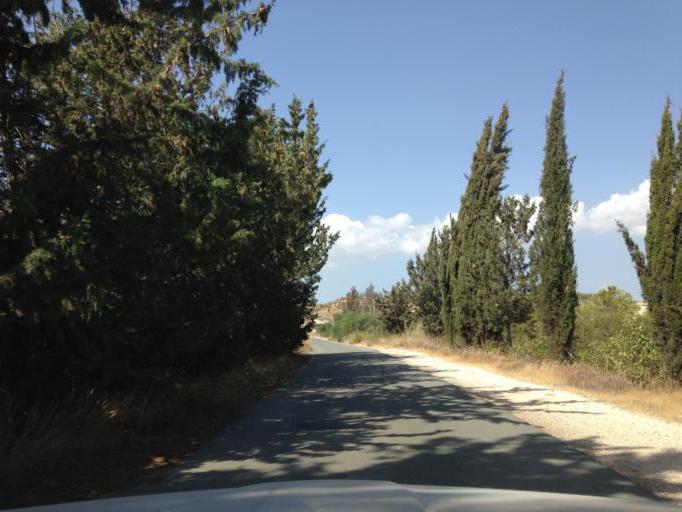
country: CY
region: Pafos
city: Mesogi
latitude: 34.7187
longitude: 32.5497
